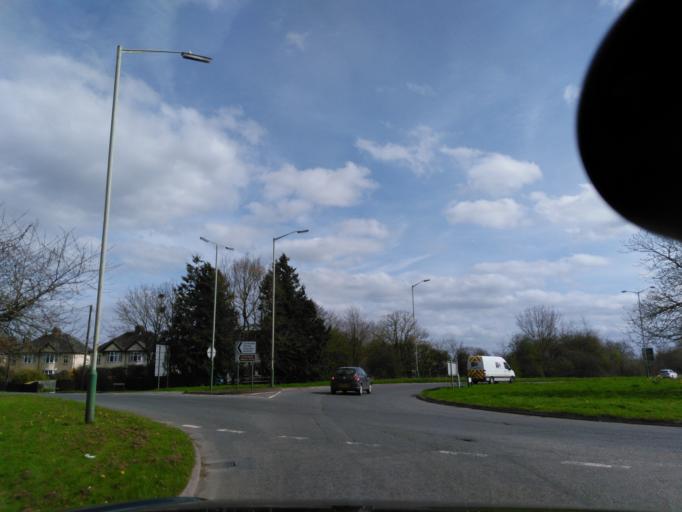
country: GB
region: England
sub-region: Wiltshire
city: Malmesbury
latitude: 51.5913
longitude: -2.0889
